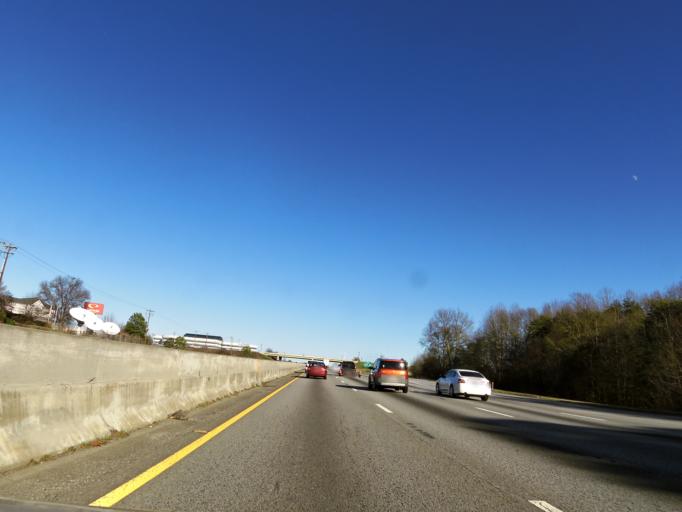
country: US
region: South Carolina
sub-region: Greenville County
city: Five Forks
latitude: 34.8571
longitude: -82.2642
